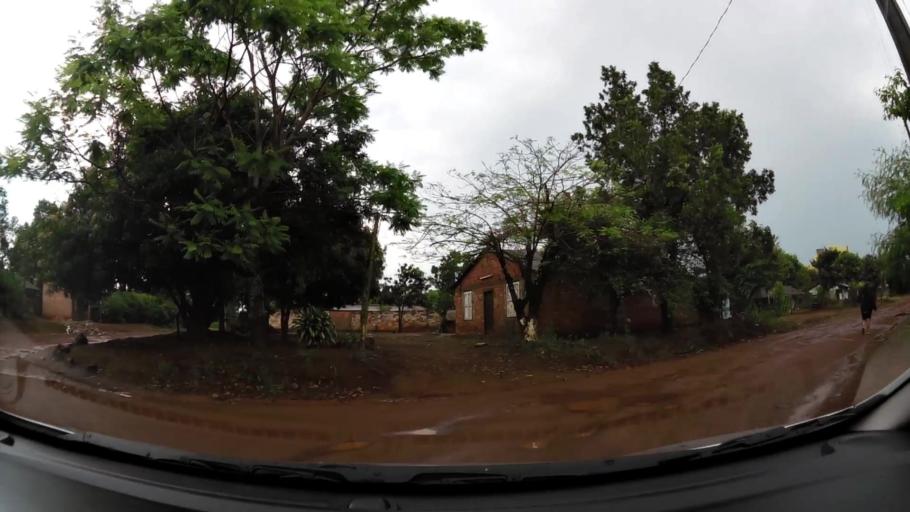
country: PY
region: Alto Parana
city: Presidente Franco
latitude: -25.5395
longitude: -54.6552
